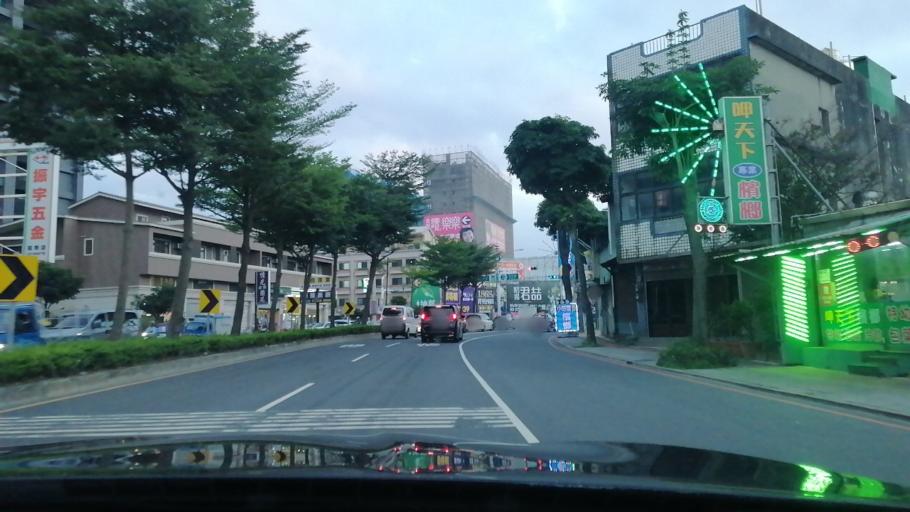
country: TW
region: Taiwan
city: Taoyuan City
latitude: 24.9992
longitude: 121.2879
